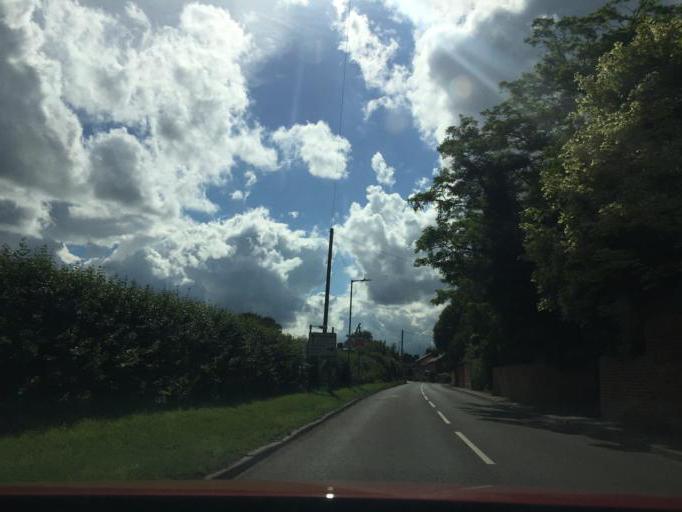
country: GB
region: England
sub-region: Hertfordshire
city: Wheathampstead
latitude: 51.8517
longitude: -0.2893
